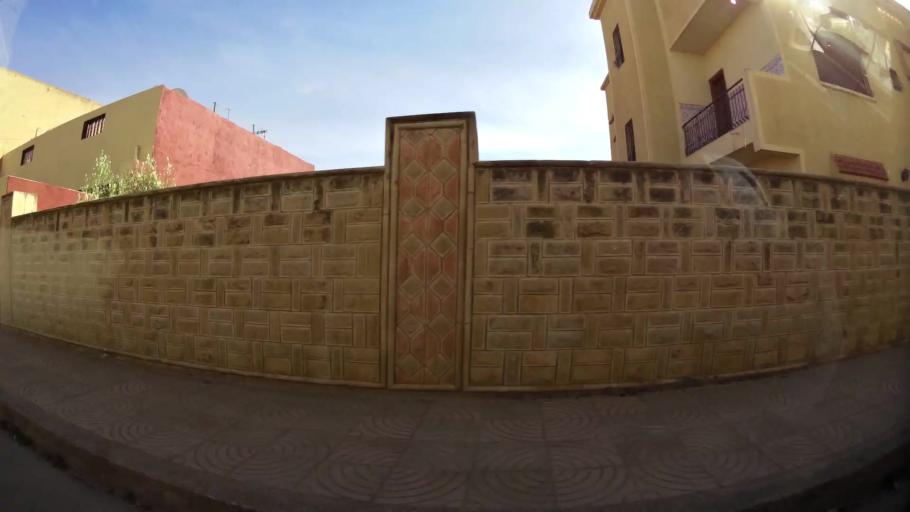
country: MA
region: Oriental
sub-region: Oujda-Angad
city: Oujda
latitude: 34.6680
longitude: -1.9155
